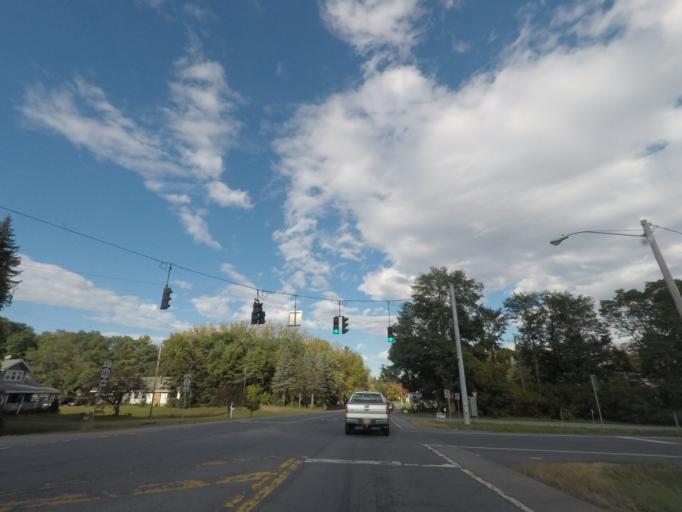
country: US
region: New York
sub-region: Schenectady County
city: Rotterdam
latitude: 42.7603
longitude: -73.9422
